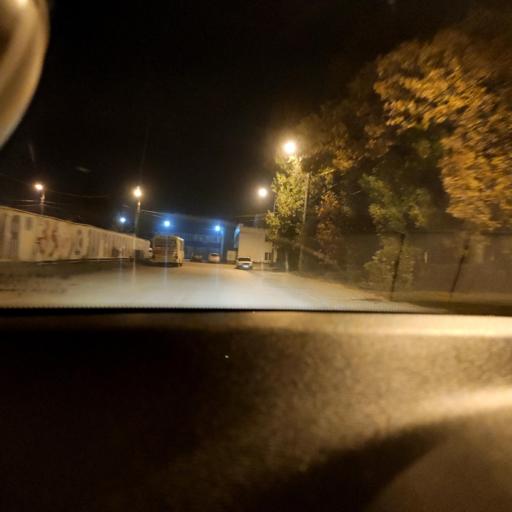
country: RU
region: Samara
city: Smyshlyayevka
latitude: 53.1898
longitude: 50.2770
